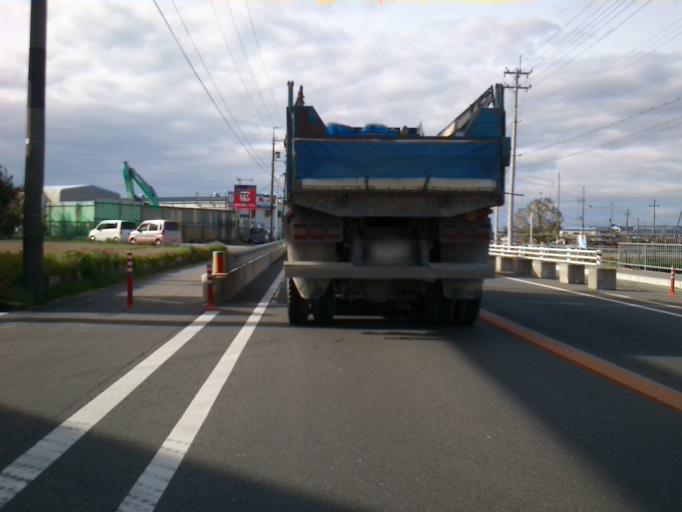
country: JP
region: Kyoto
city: Tanabe
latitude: 34.7643
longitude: 135.8095
